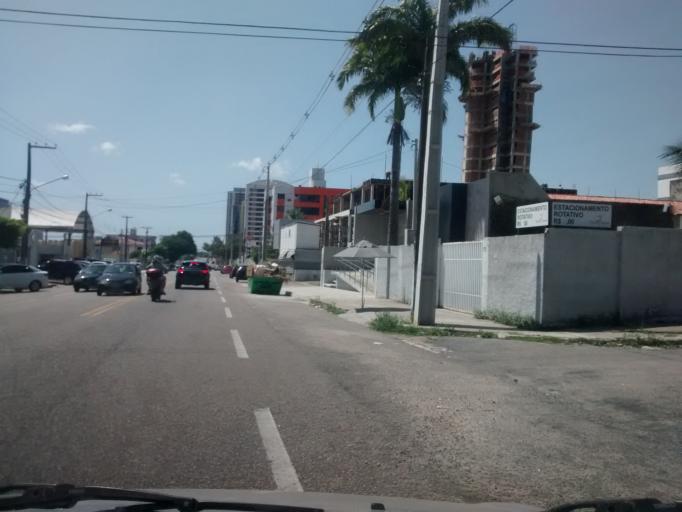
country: BR
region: Rio Grande do Norte
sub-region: Natal
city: Natal
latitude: -5.8225
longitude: -35.2171
